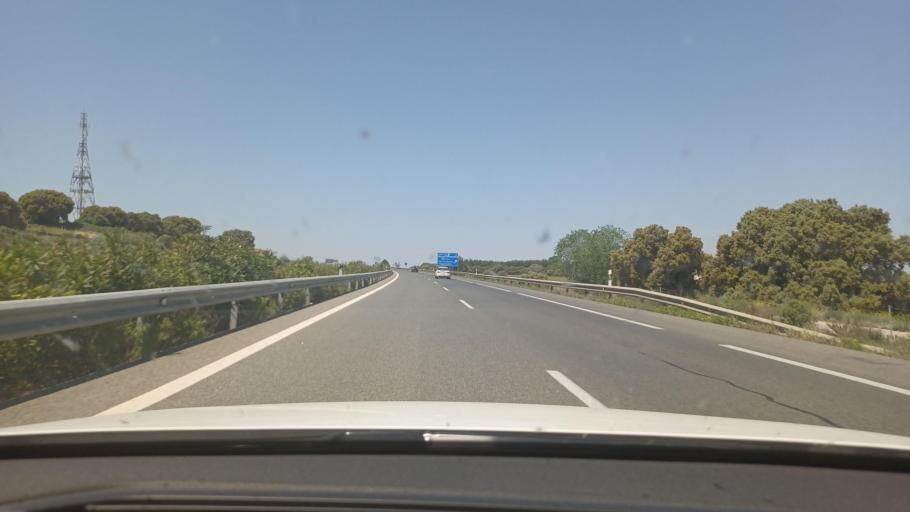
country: ES
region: Castille-La Mancha
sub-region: Provincia de Albacete
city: Corral-Rubio
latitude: 38.9005
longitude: -1.4737
